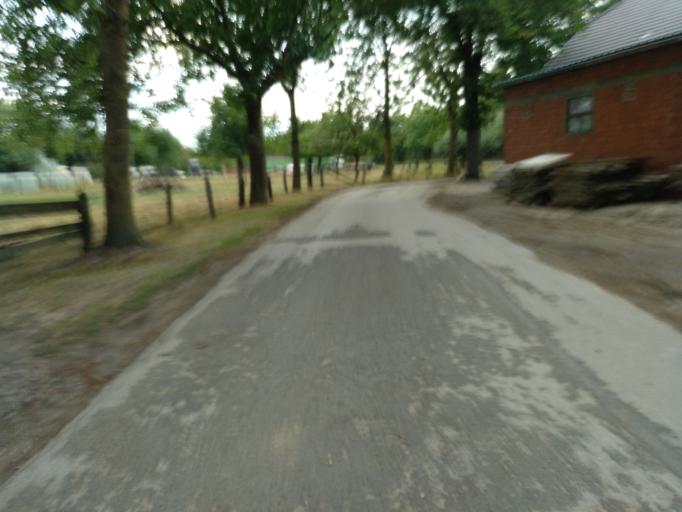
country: DE
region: North Rhine-Westphalia
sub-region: Regierungsbezirk Dusseldorf
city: Krefeld
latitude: 51.4040
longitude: 6.5449
